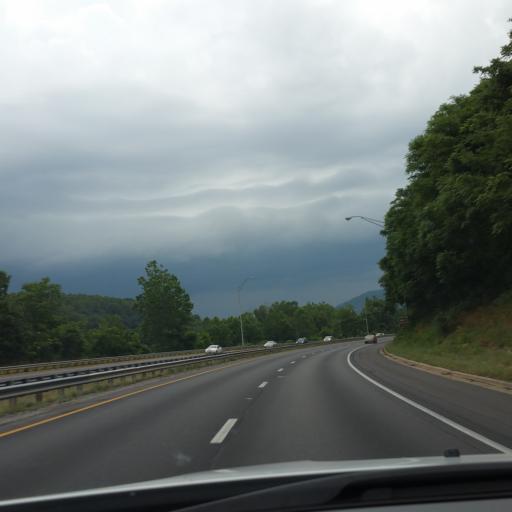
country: US
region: North Carolina
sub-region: Buncombe County
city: Asheville
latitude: 35.6063
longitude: -82.5771
